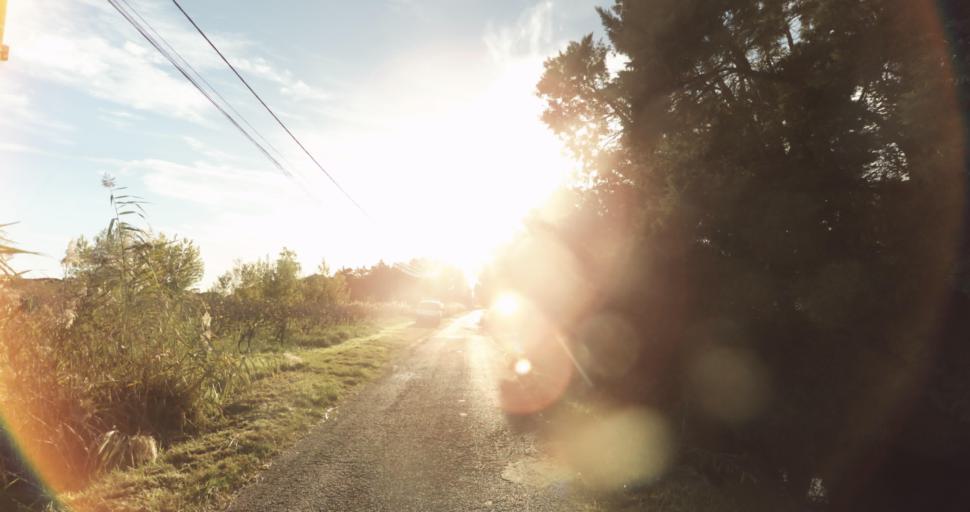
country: FR
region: Languedoc-Roussillon
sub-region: Departement du Gard
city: Aigues-Mortes
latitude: 43.5605
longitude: 4.2003
